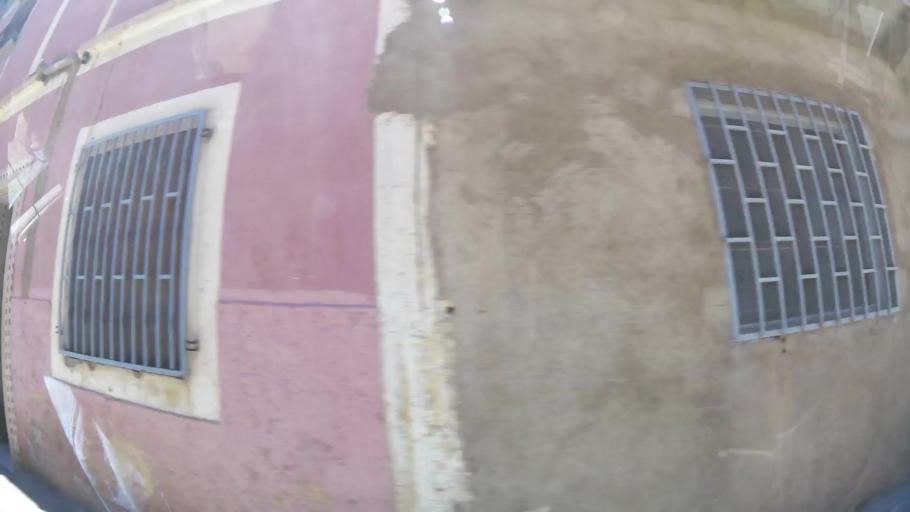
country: MA
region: Oriental
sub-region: Oujda-Angad
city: Oujda
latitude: 34.6602
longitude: -1.9222
